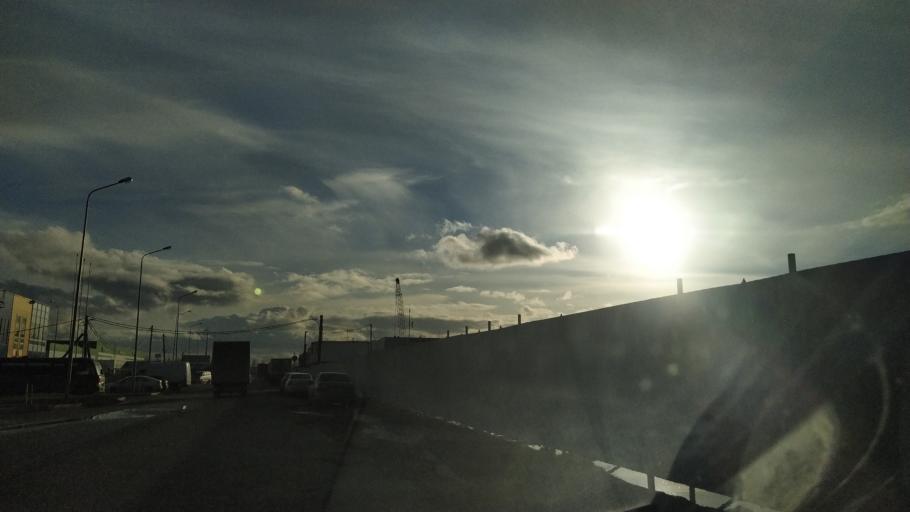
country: RU
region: St.-Petersburg
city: Petro-Slavyanka
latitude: 59.7772
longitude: 30.4641
